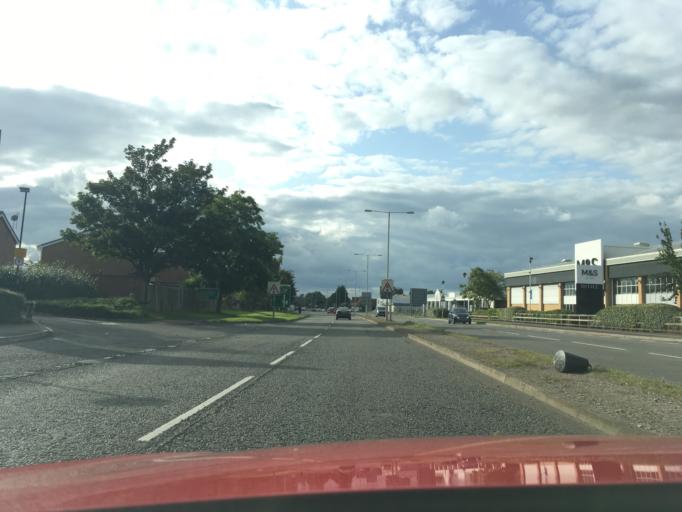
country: GB
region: England
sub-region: Gloucestershire
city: Swindon
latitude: 51.9144
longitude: -2.1006
